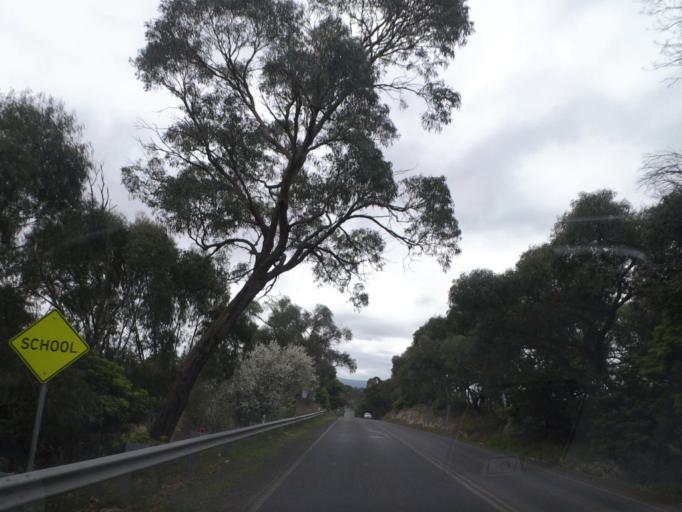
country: AU
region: Victoria
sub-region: Nillumbik
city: Doreen
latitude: -37.6162
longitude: 145.1364
